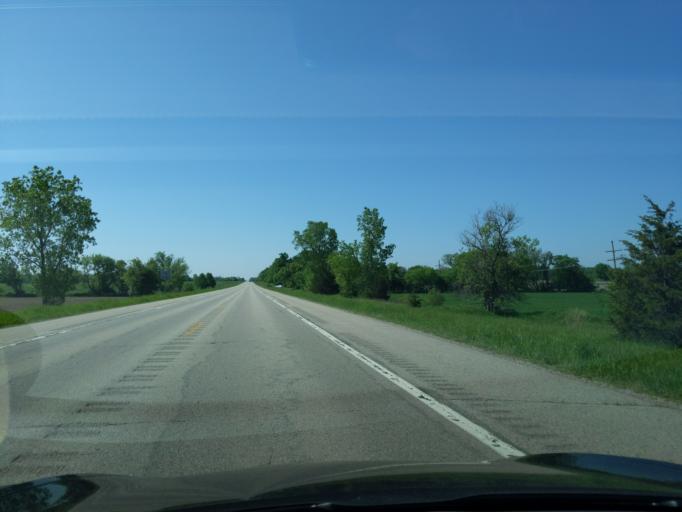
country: US
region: Michigan
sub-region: Ingham County
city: Stockbridge
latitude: 42.5494
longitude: -84.1916
